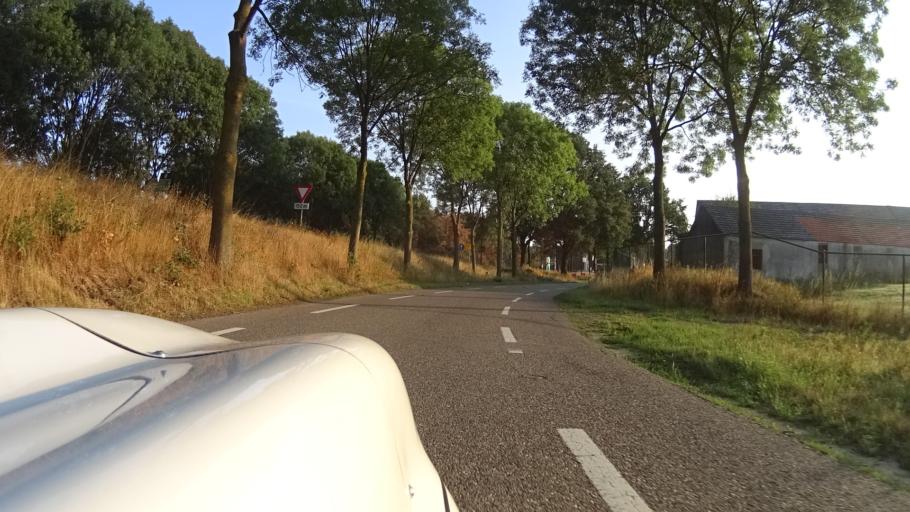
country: NL
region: Limburg
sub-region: Gemeente Bergen
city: Wellerlooi
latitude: 51.5533
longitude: 6.0982
